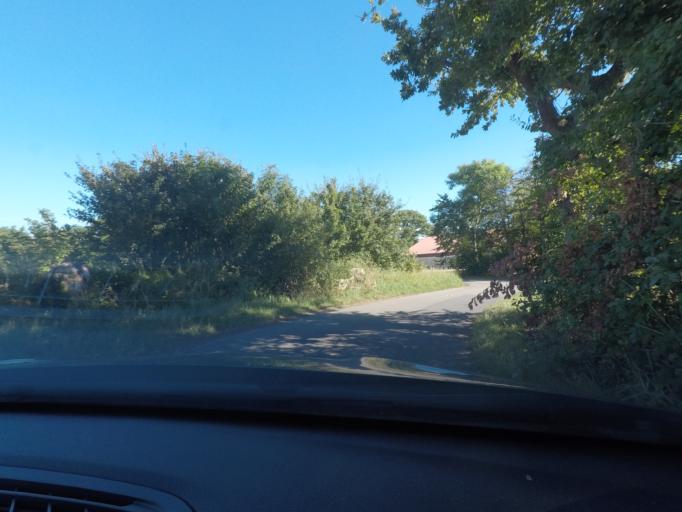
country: DK
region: Zealand
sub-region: Lolland Kommune
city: Maribo
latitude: 54.9814
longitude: 11.5275
